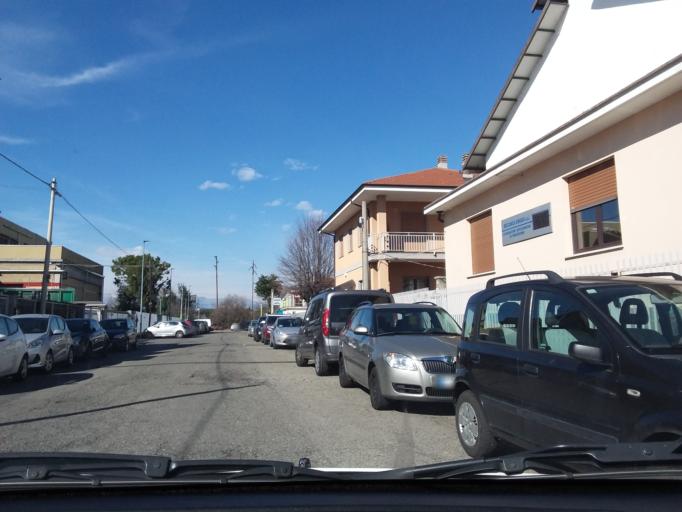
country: IT
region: Piedmont
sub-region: Provincia di Torino
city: Collegno
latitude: 45.0806
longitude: 7.5566
